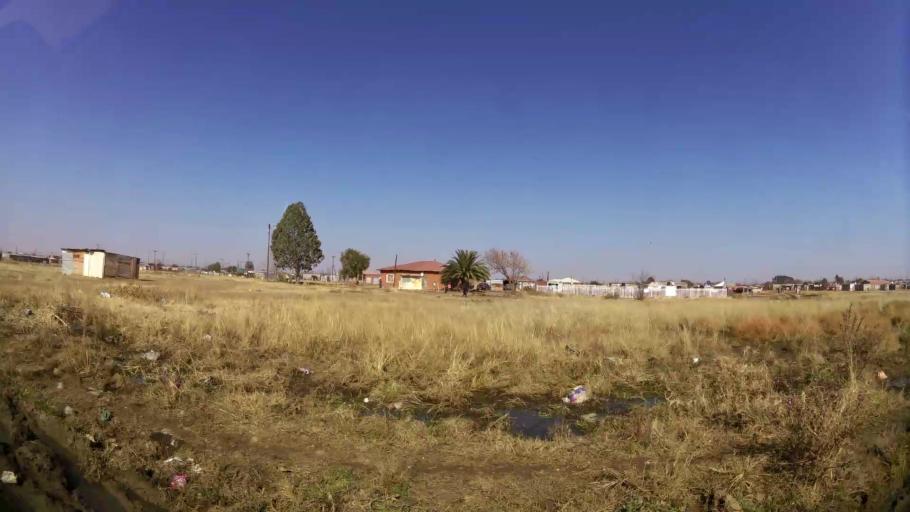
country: ZA
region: Orange Free State
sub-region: Mangaung Metropolitan Municipality
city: Bloemfontein
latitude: -29.1735
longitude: 26.2850
